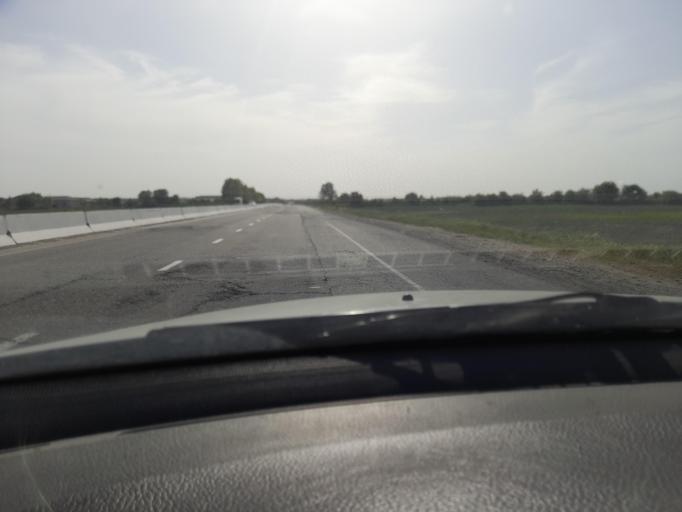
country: UZ
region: Samarqand
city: Kattaqo'rg'on
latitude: 39.9207
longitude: 66.3455
